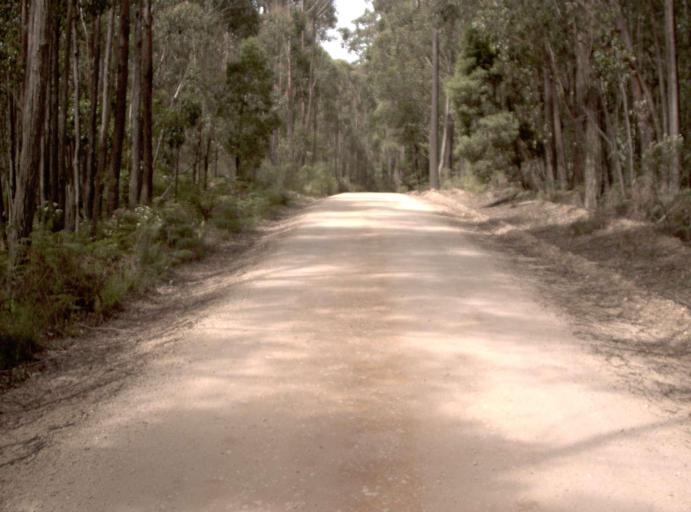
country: AU
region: Victoria
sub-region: East Gippsland
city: Lakes Entrance
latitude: -37.6208
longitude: 148.6829
